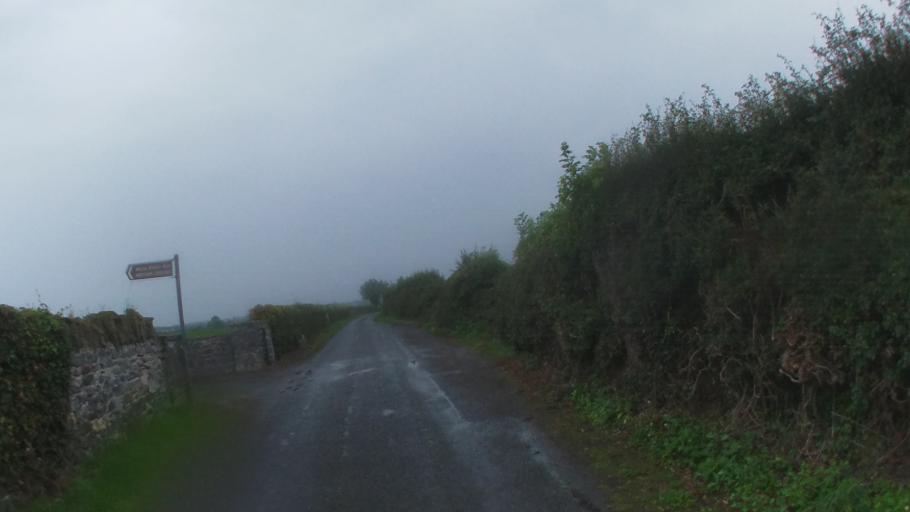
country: IE
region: Leinster
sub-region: Kilkenny
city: Callan
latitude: 52.5451
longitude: -7.3154
